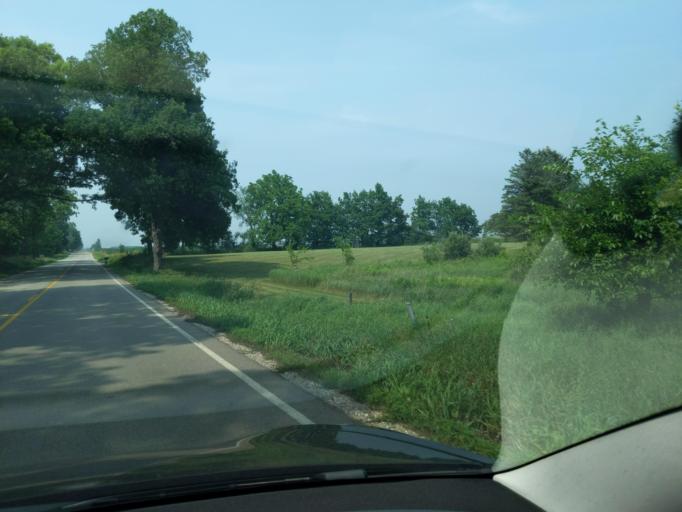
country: US
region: Michigan
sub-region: Clinton County
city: DeWitt
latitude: 42.9063
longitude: -84.5773
